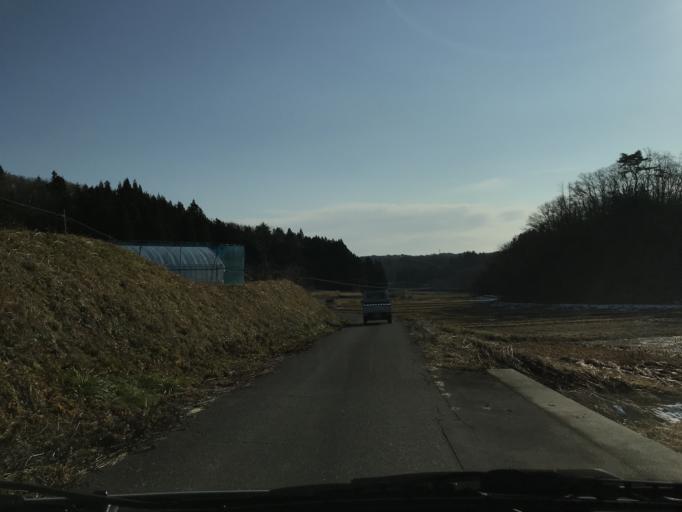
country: JP
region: Iwate
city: Ichinoseki
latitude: 38.9720
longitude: 141.0566
